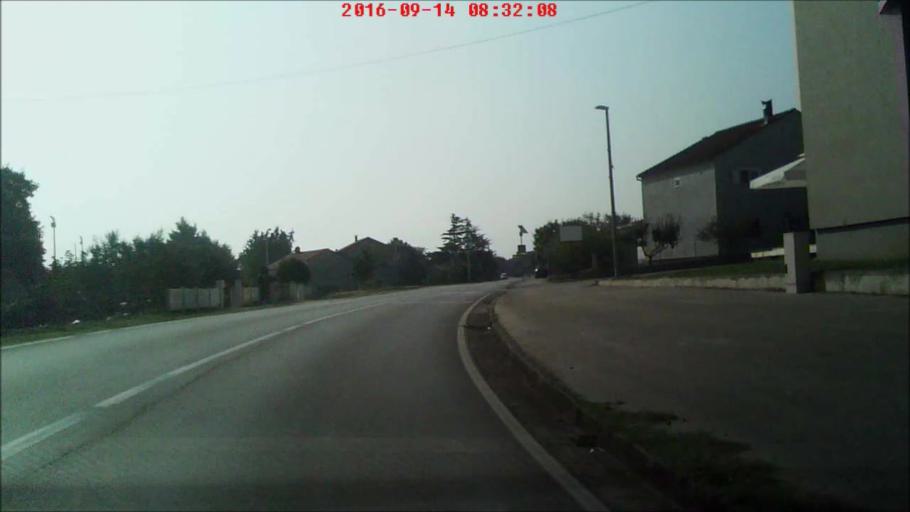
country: HR
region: Zadarska
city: Policnik
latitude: 44.1653
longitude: 15.3048
